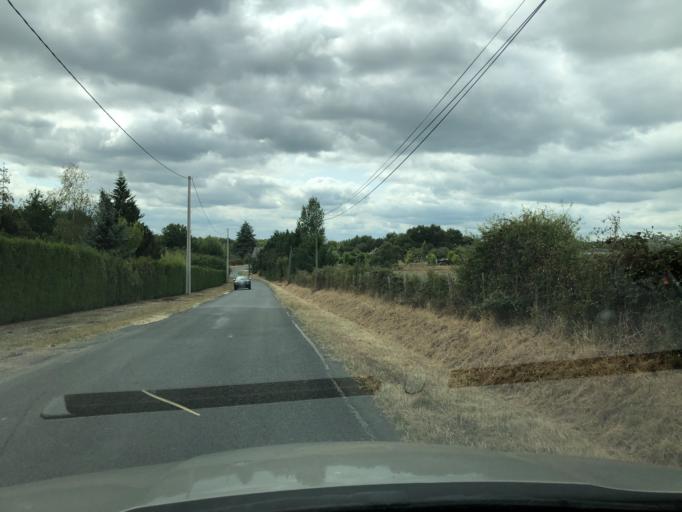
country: FR
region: Centre
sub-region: Departement d'Indre-et-Loire
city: Mazieres-de-Touraine
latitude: 47.3923
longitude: 0.4586
